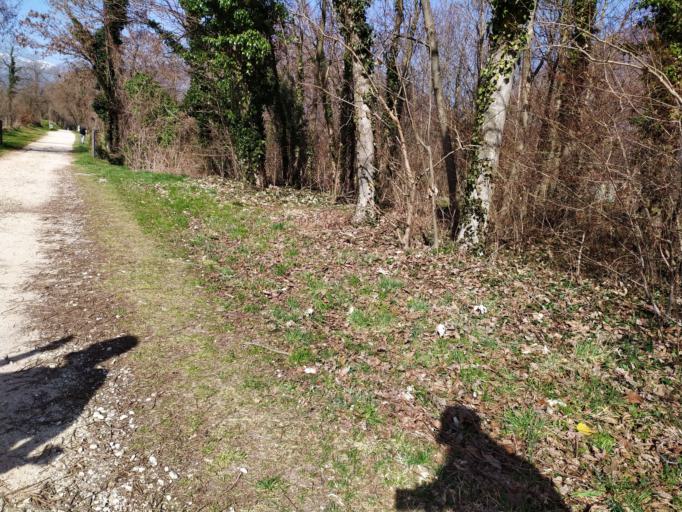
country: IT
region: Veneto
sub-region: Provincia di Vicenza
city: Velo d'Astico
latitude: 45.7888
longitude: 11.3818
